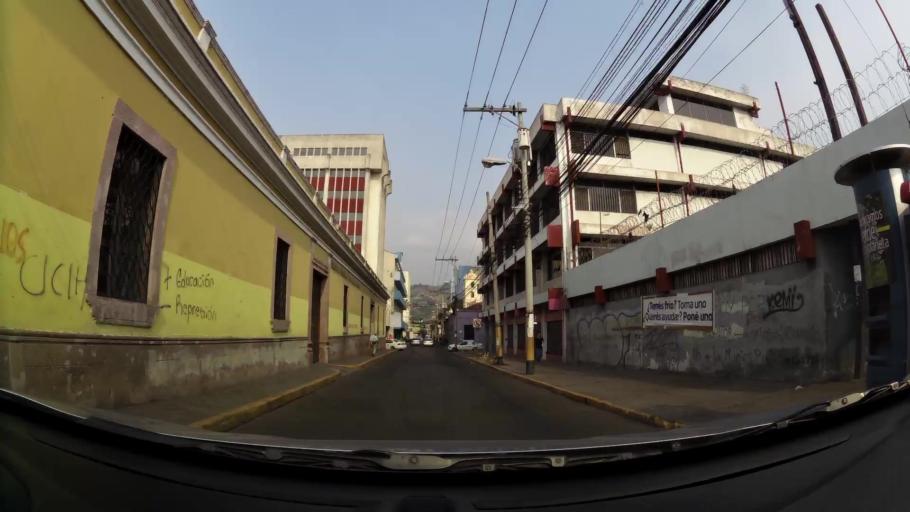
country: HN
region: Francisco Morazan
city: Tegucigalpa
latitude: 14.1051
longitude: -87.2028
